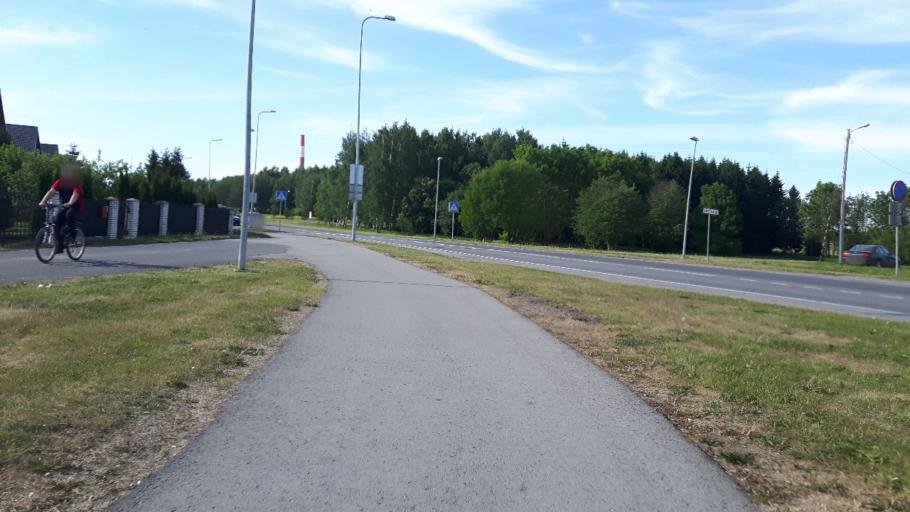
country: EE
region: Harju
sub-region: Joelaehtme vald
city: Loo
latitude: 59.4361
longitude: 24.9415
